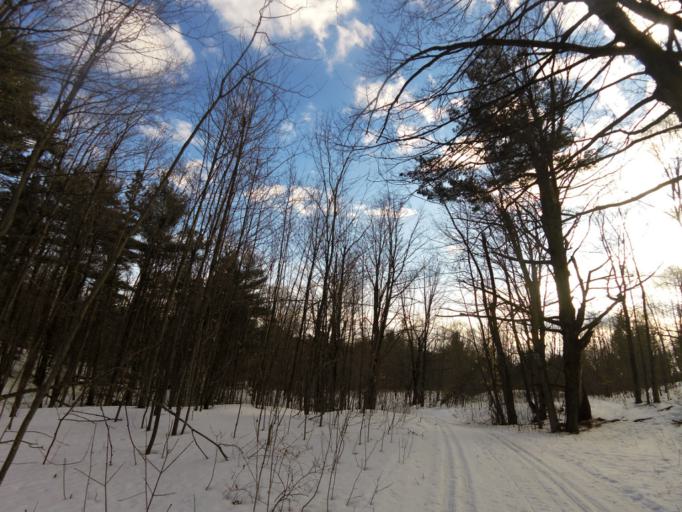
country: CA
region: Quebec
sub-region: Outaouais
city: Gatineau
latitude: 45.4815
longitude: -75.8467
